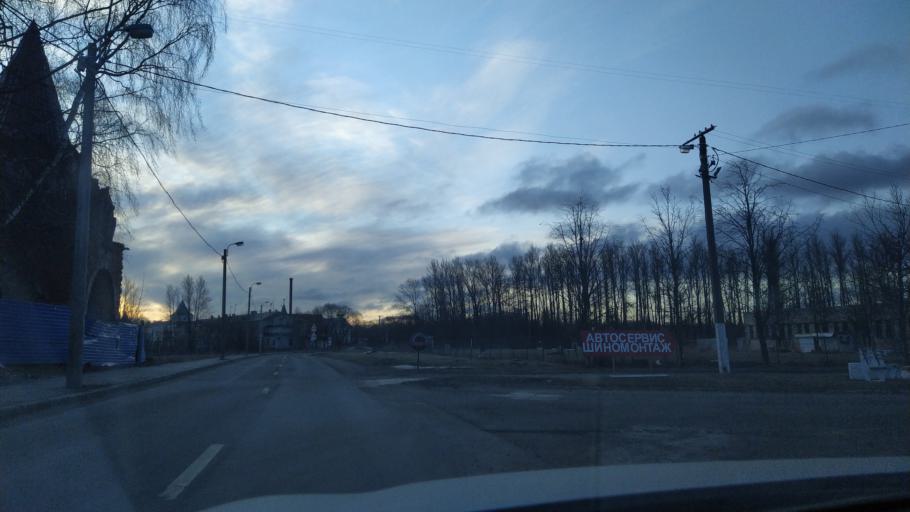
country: RU
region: St.-Petersburg
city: Pushkin
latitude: 59.7313
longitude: 30.3837
